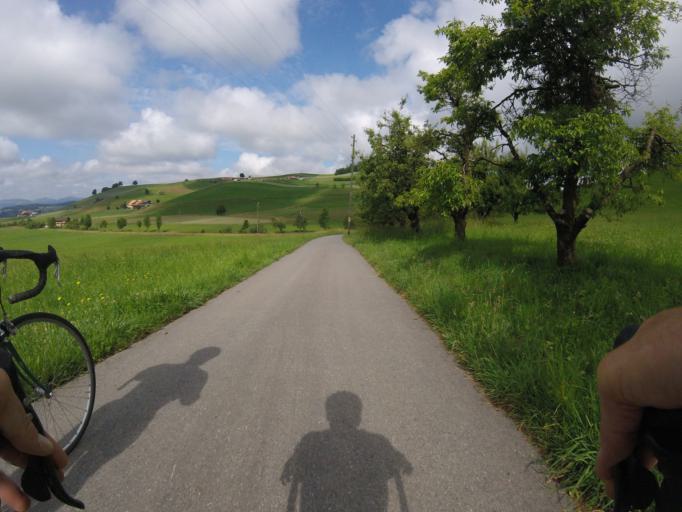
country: CH
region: Bern
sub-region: Bern-Mittelland District
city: Vechigen
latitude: 46.9720
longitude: 7.5832
